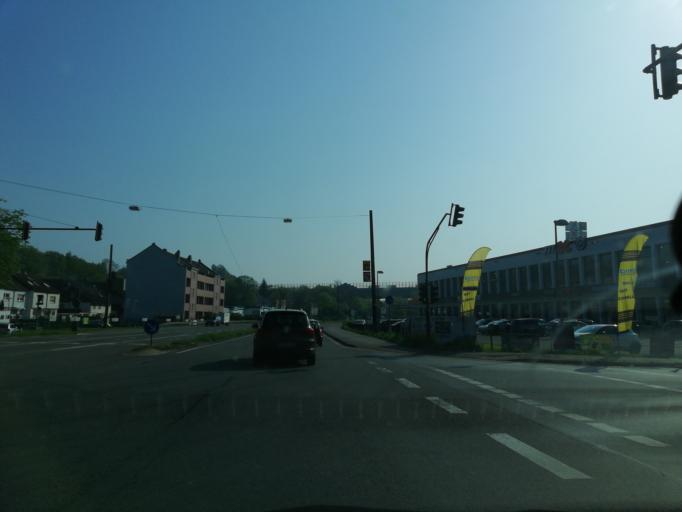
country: DE
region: North Rhine-Westphalia
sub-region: Regierungsbezirk Arnsberg
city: Schwelm
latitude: 51.2826
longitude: 7.2533
